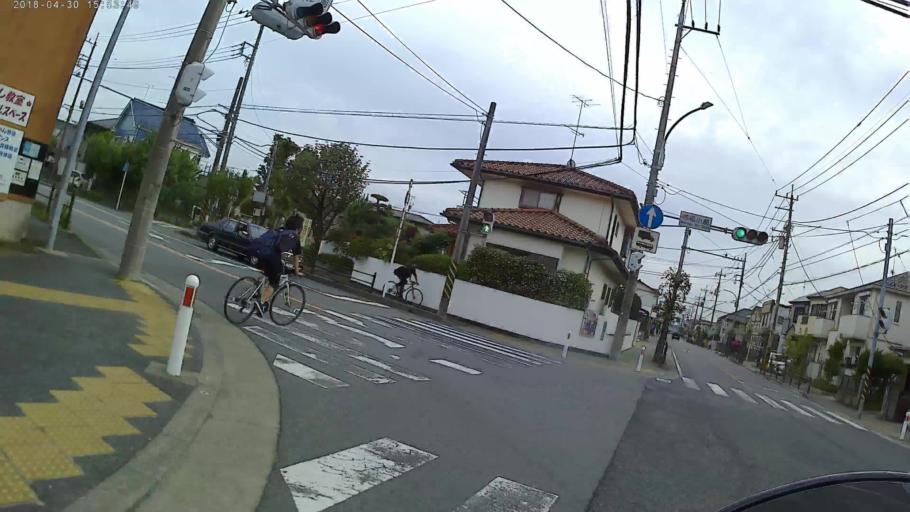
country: JP
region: Tokyo
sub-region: Machida-shi
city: Machida
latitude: 35.5408
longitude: 139.4284
